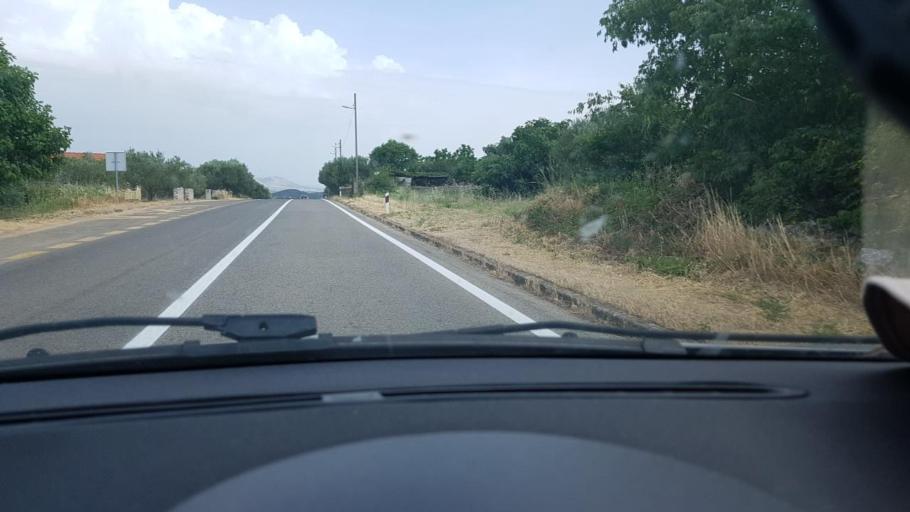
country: HR
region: Sibensko-Kniniska
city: Zaton
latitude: 43.8549
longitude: 15.7594
